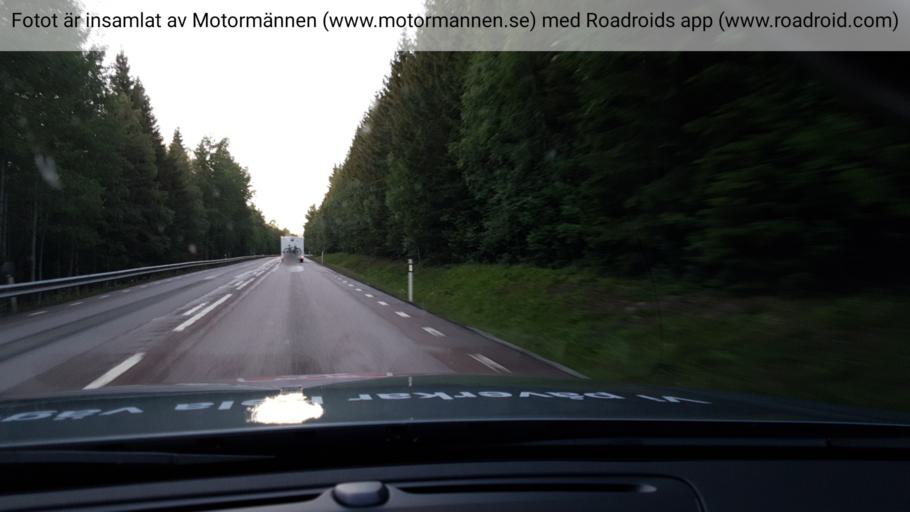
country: SE
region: Vaestmanland
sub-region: Fagersta Kommun
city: Fagersta
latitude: 59.9349
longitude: 15.7303
